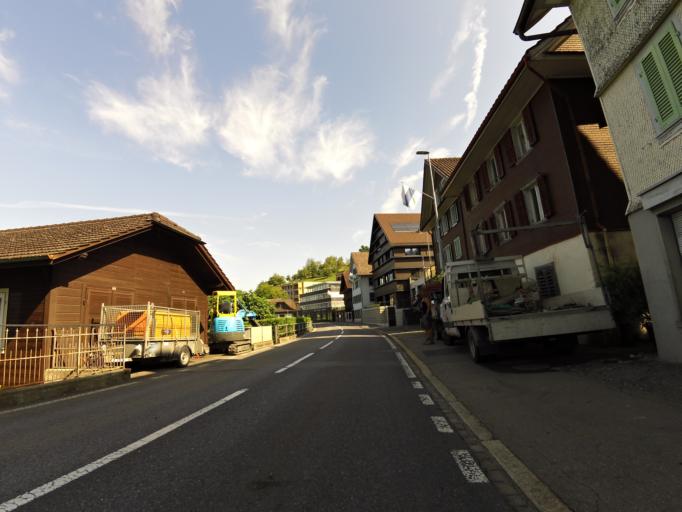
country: CH
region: Zug
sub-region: Zug
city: Walchwil
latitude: 47.1000
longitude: 8.5128
